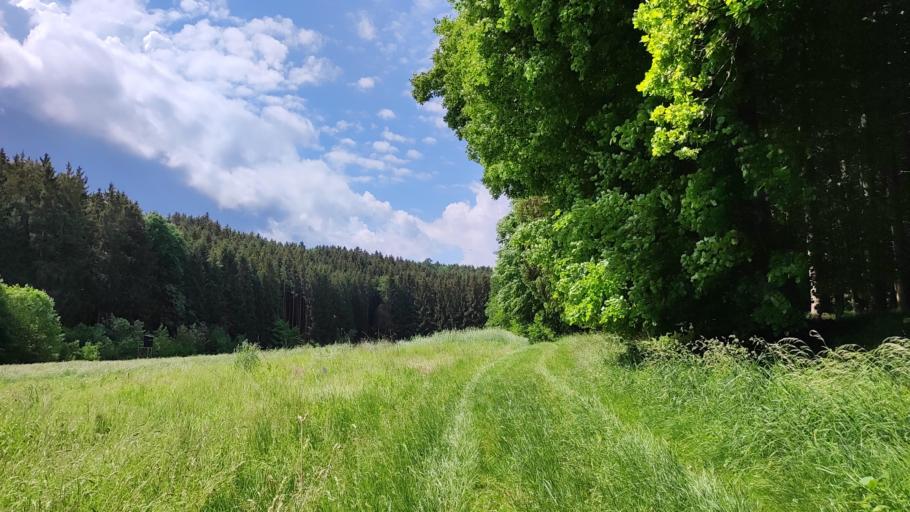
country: DE
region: Bavaria
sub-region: Swabia
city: Zusmarshausen
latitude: 48.4302
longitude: 10.5816
